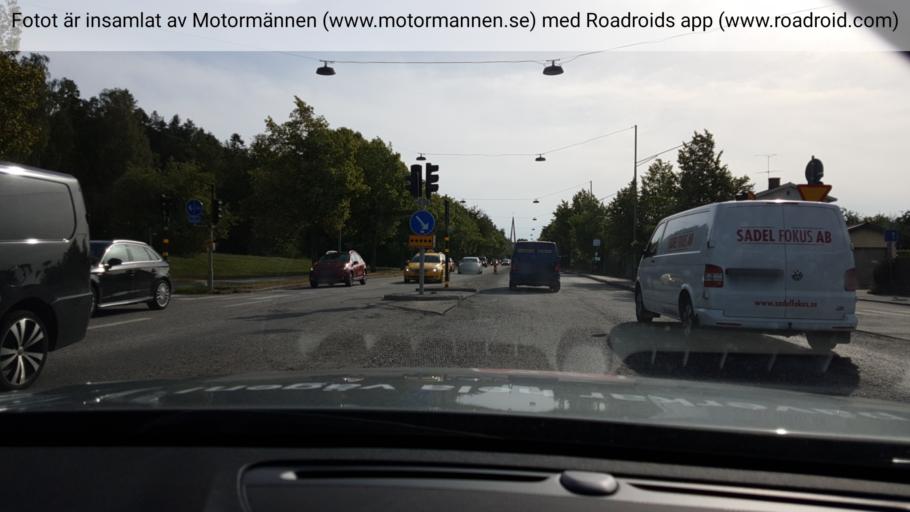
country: SE
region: Stockholm
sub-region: Stockholms Kommun
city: Bromma
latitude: 59.3334
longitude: 17.9252
